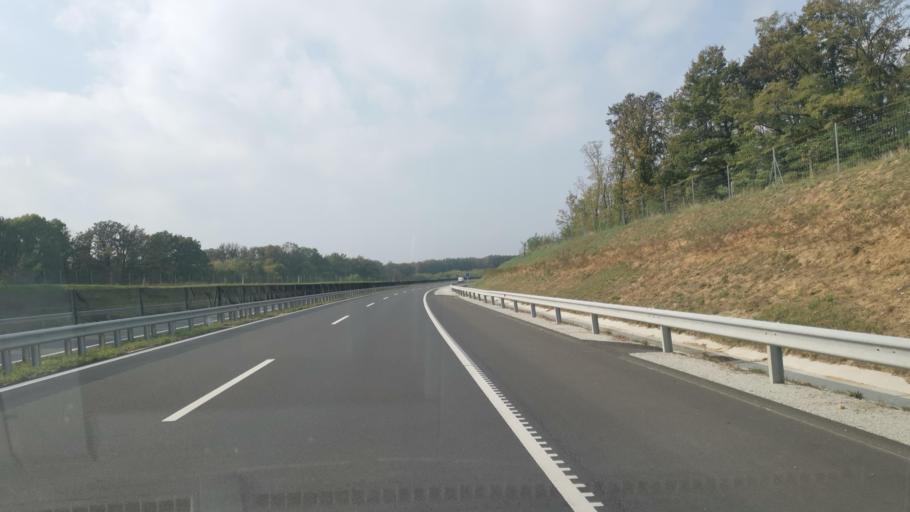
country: AT
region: Burgenland
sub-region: Politischer Bezirk Oberpullendorf
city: Deutschkreutz
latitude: 47.6290
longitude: 16.6392
